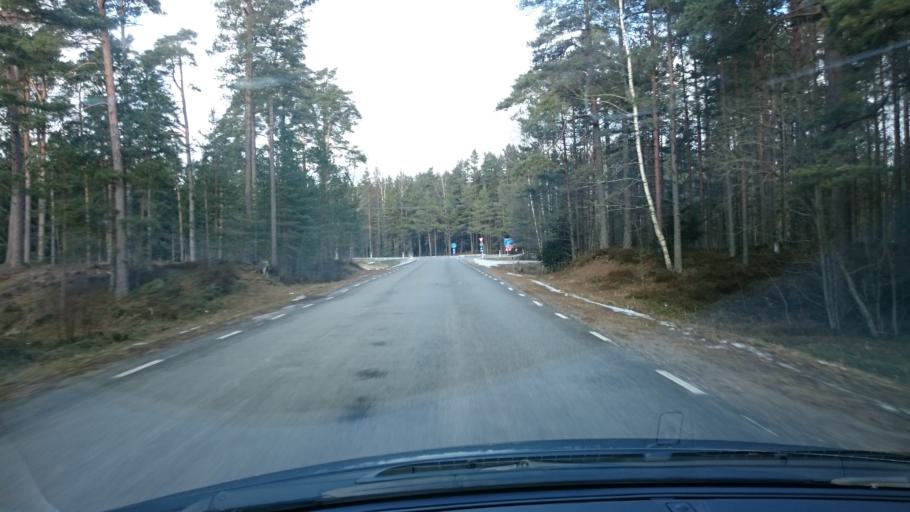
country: EE
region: Harju
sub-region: Keila linn
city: Keila
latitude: 59.3918
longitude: 24.2943
